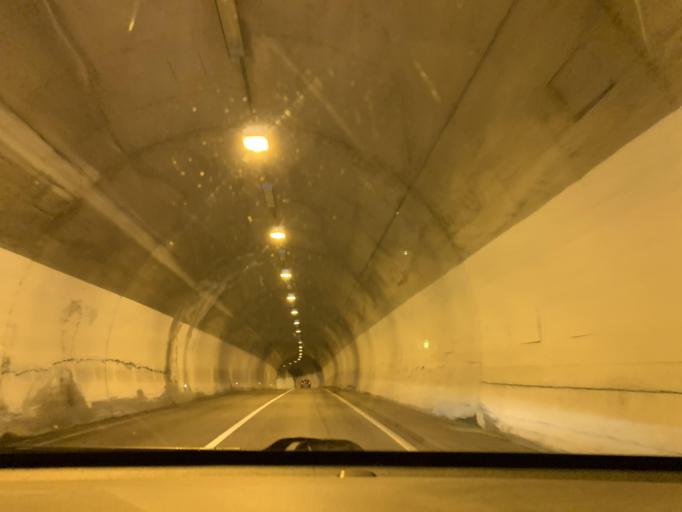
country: IT
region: Trentino-Alto Adige
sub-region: Bolzano
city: Avelengo
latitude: 46.6457
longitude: 11.2251
